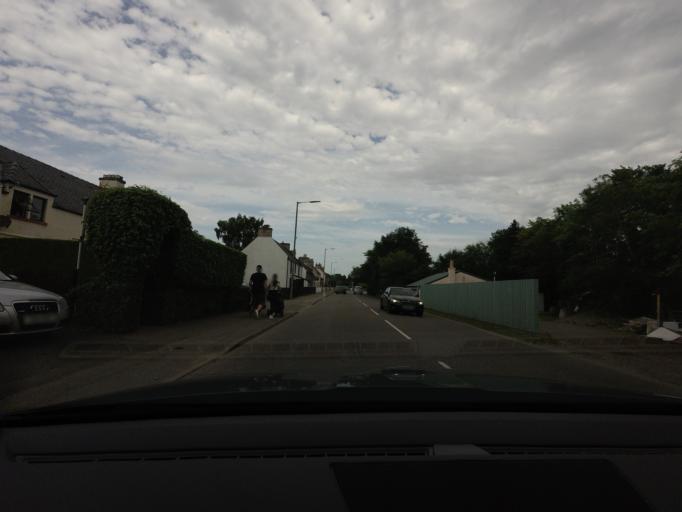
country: GB
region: Scotland
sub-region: Highland
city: Alness
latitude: 57.6949
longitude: -4.2634
